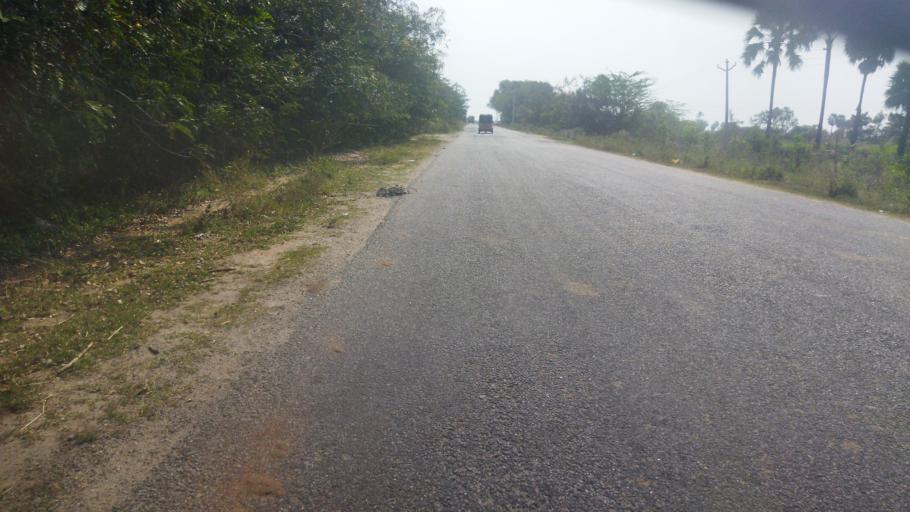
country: IN
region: Telangana
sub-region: Nalgonda
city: Nalgonda
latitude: 17.1040
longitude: 79.2820
